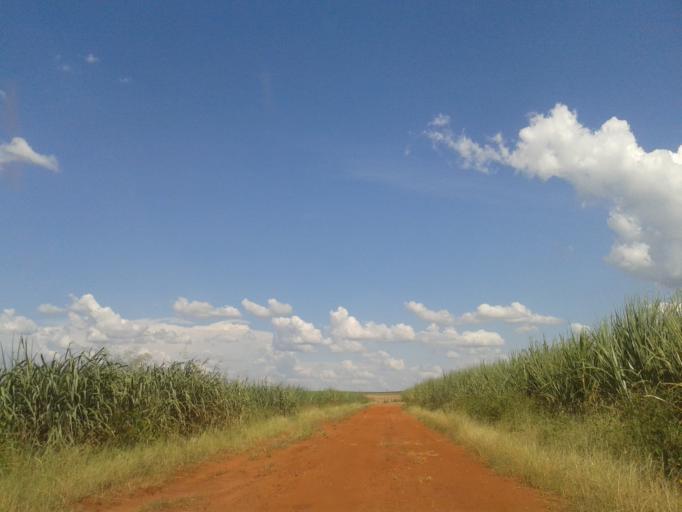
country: BR
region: Minas Gerais
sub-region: Santa Vitoria
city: Santa Vitoria
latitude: -19.1153
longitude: -50.4081
